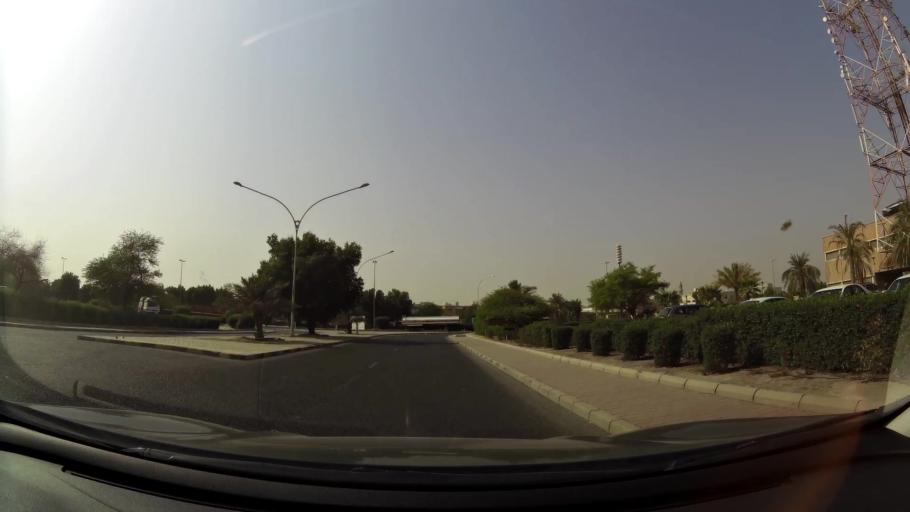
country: KW
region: Al Asimah
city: Ar Rabiyah
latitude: 29.2871
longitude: 47.8833
